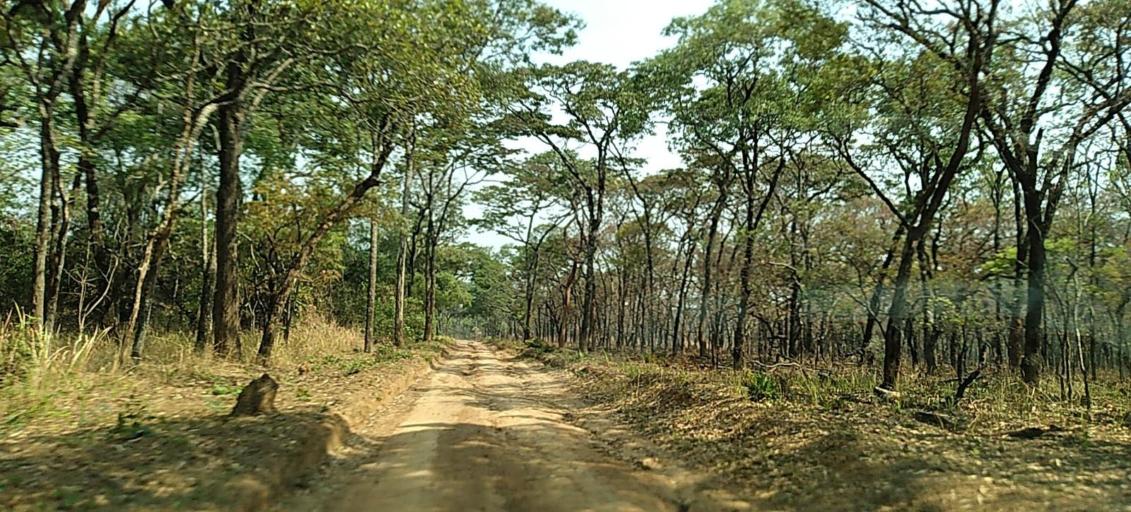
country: ZM
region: North-Western
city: Kansanshi
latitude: -12.0587
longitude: 26.8876
